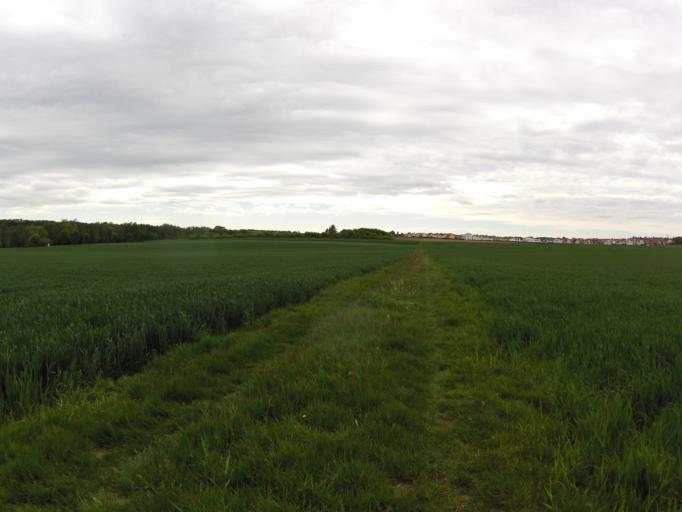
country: DE
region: Bavaria
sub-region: Regierungsbezirk Unterfranken
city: Unterpleichfeld
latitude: 49.8499
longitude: 10.0618
